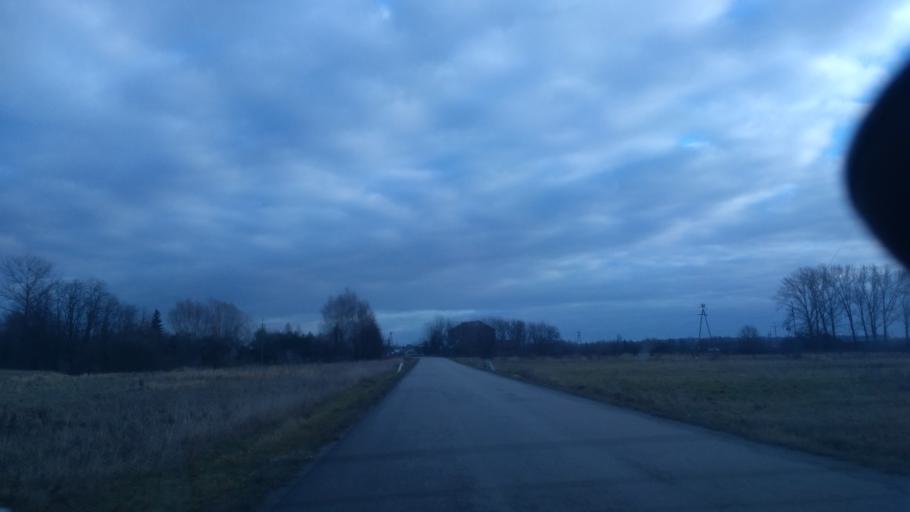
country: PL
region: Subcarpathian Voivodeship
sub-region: Powiat lancucki
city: Czarna
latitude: 50.0946
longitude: 22.1652
